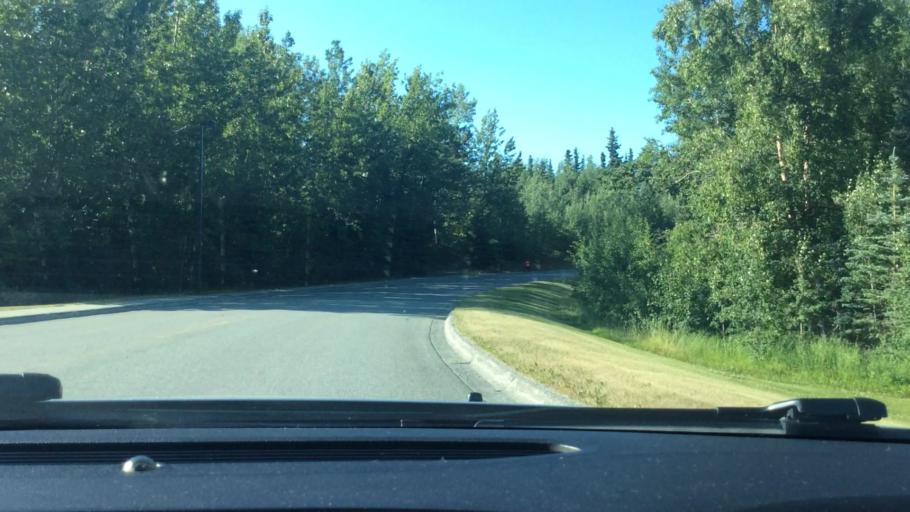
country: US
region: Alaska
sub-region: Anchorage Municipality
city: Elmendorf Air Force Base
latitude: 61.2486
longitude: -149.7017
